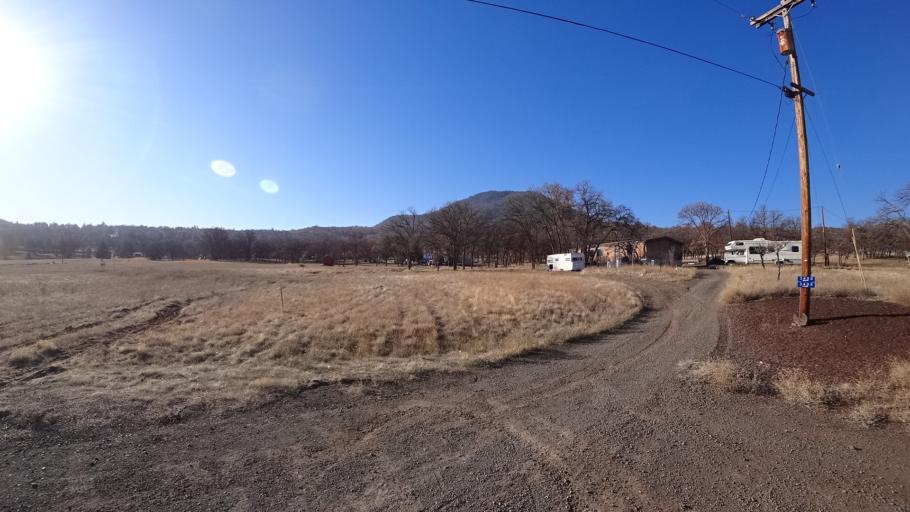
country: US
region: California
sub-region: Siskiyou County
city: Montague
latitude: 41.8899
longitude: -122.4925
